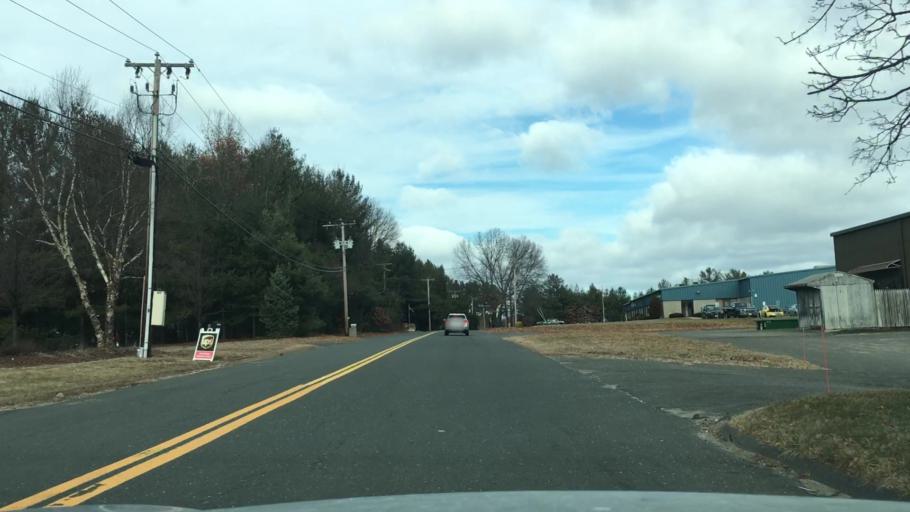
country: US
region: Massachusetts
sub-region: Hampden County
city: Southwick
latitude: 42.0654
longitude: -72.7463
